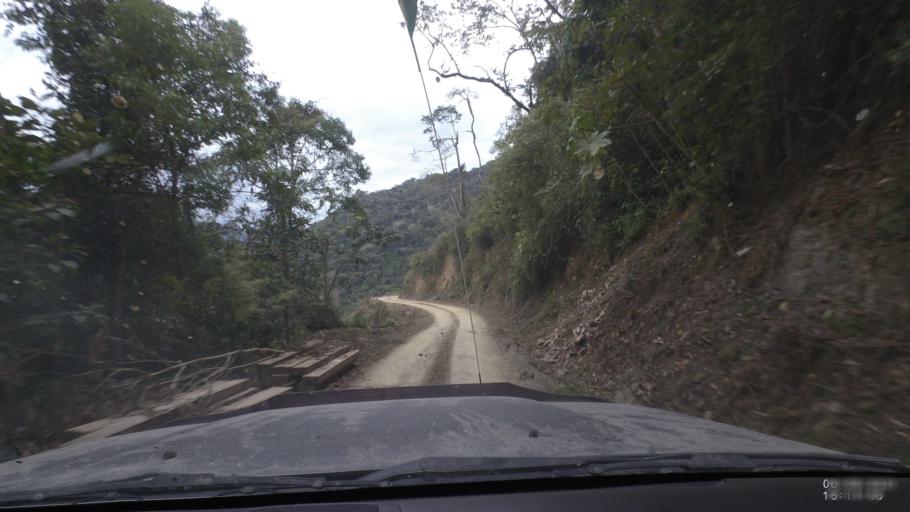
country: BO
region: La Paz
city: Quime
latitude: -16.5532
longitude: -66.7354
